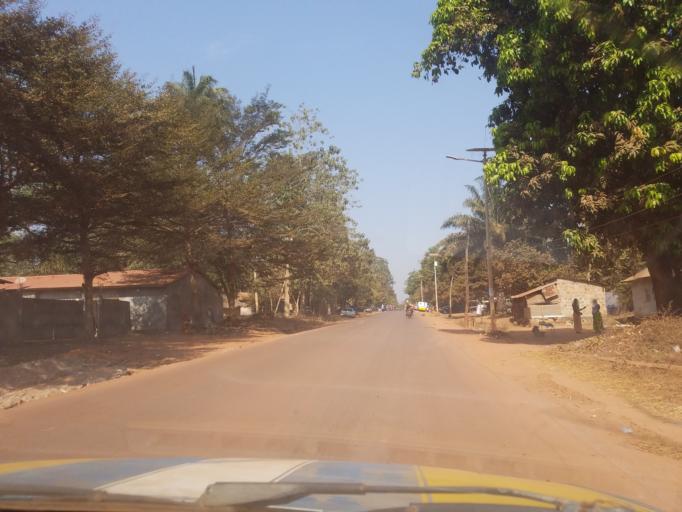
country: GN
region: Boke
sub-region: Boke Prefecture
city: Sangueya
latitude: 10.8040
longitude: -14.3900
